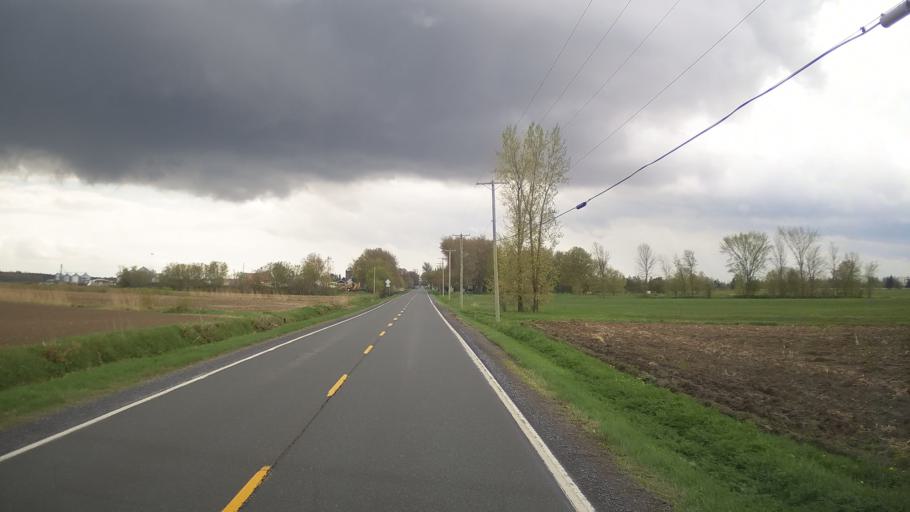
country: CA
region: Quebec
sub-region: Monteregie
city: Farnham
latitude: 45.3097
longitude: -73.1100
